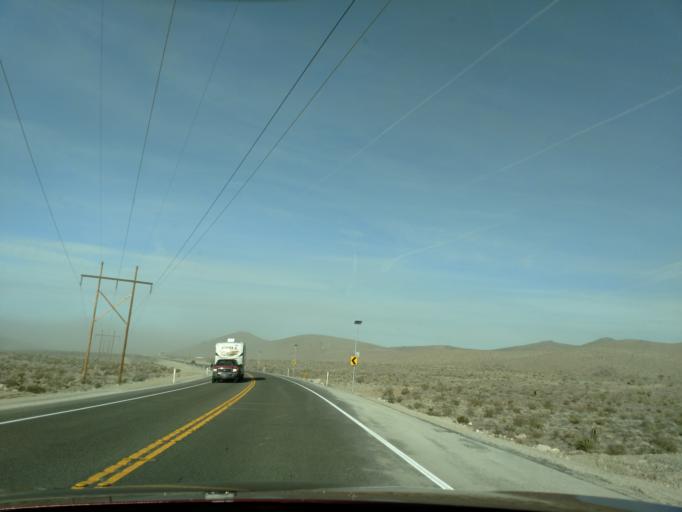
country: US
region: Nevada
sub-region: Nye County
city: Pahrump
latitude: 36.4350
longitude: -116.0746
